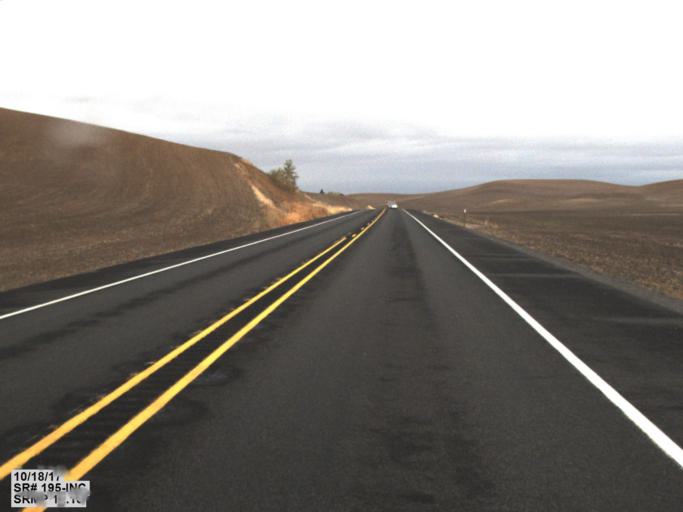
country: US
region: Washington
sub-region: Whitman County
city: Pullman
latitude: 46.6061
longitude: -117.1643
